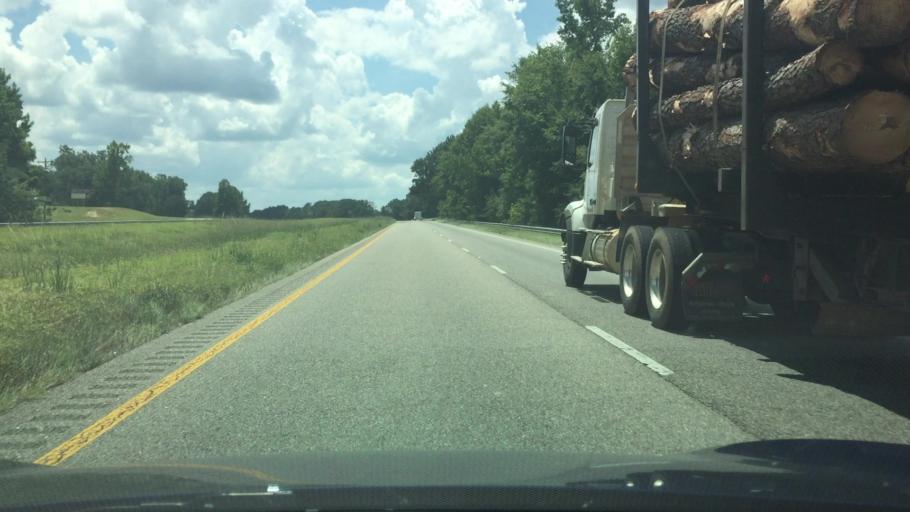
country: US
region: Alabama
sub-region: Montgomery County
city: Taylor
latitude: 32.0795
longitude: -86.0636
